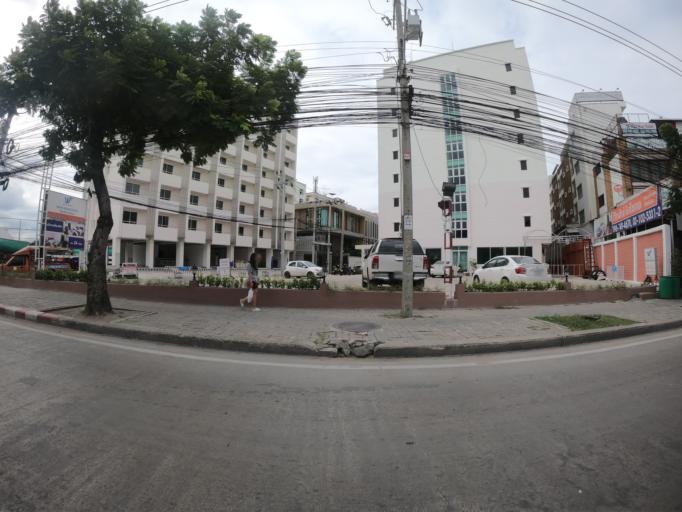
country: TH
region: Bangkok
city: Bang Na
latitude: 13.6770
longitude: 100.6570
